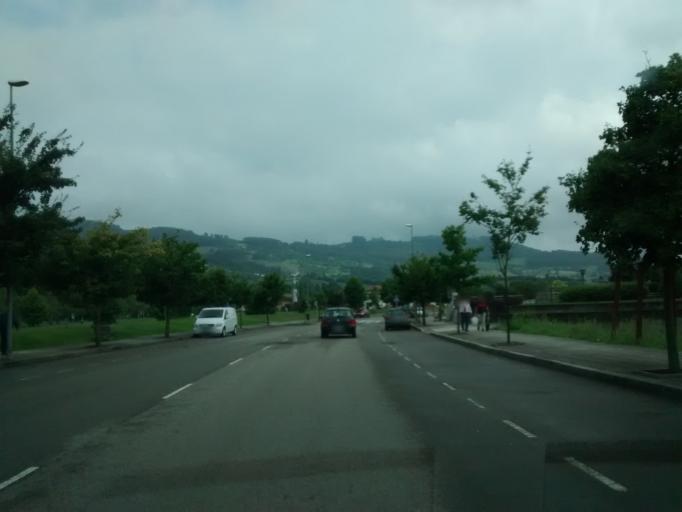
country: ES
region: Asturias
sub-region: Province of Asturias
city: Villaviciosa
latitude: 43.4812
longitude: -5.4400
